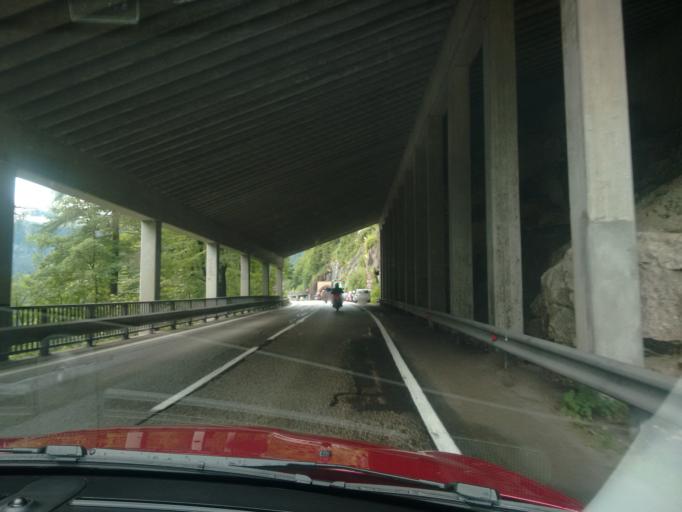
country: AT
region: Upper Austria
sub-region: Politischer Bezirk Gmunden
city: Bad Goisern
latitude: 47.5697
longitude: 13.6498
